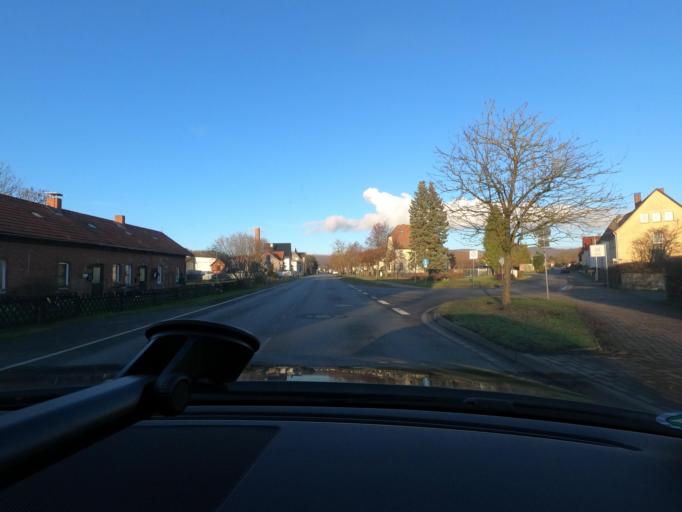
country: DE
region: Lower Saxony
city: Herzberg am Harz
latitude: 51.6455
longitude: 10.3308
